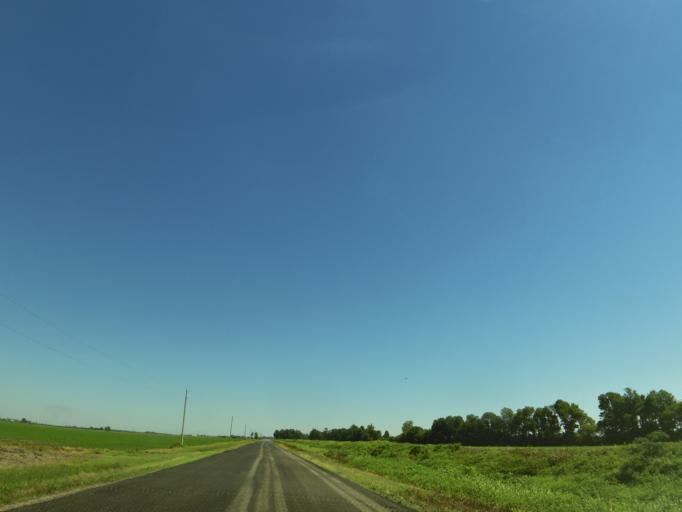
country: US
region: Missouri
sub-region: New Madrid County
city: Lilbourn
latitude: 36.5603
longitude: -89.7027
